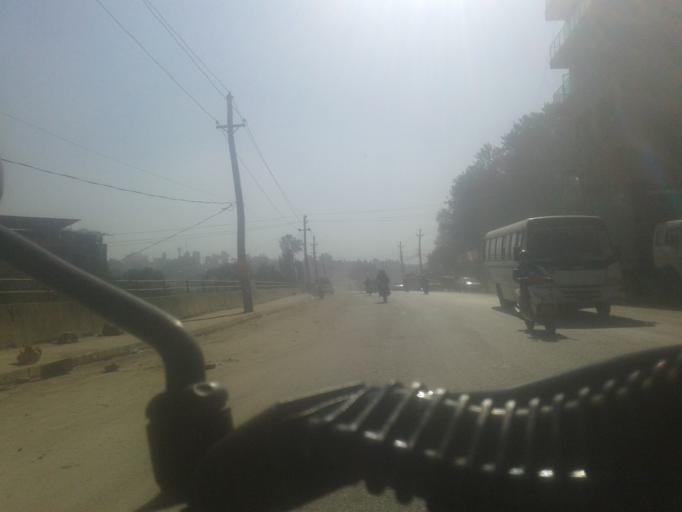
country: NP
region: Central Region
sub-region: Bagmati Zone
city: Patan
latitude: 27.6838
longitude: 85.2977
